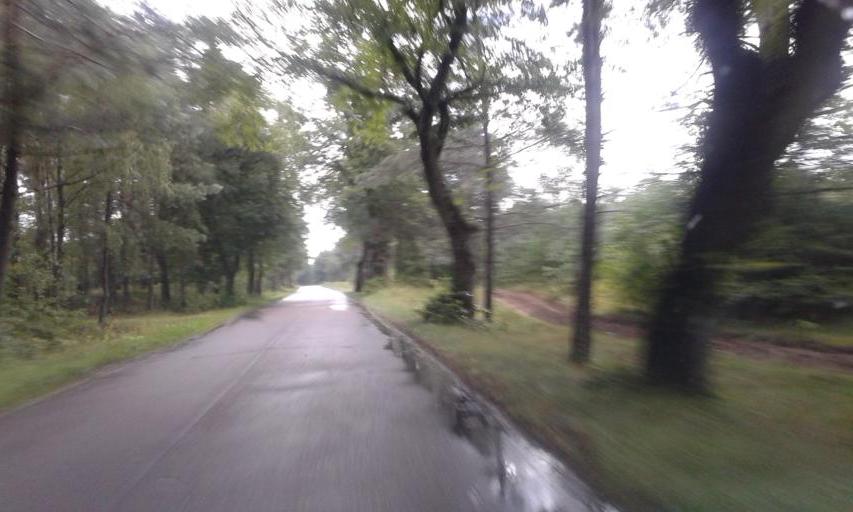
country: PL
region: West Pomeranian Voivodeship
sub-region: Powiat szczecinecki
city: Borne Sulinowo
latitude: 53.5017
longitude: 16.5003
